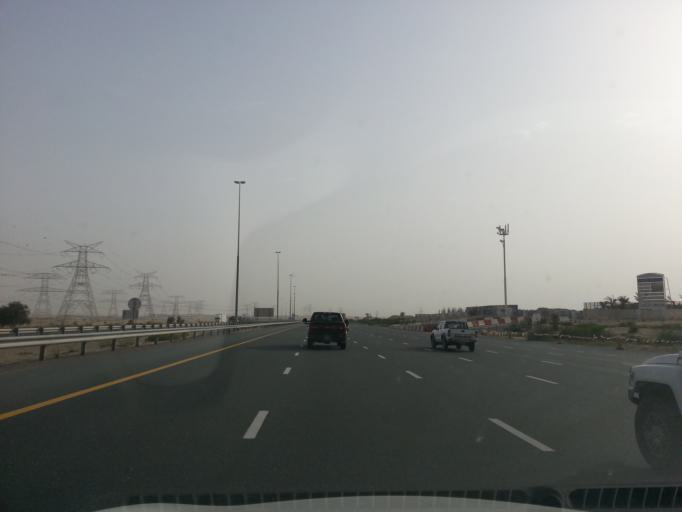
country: AE
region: Dubai
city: Dubai
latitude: 24.9971
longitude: 55.2540
